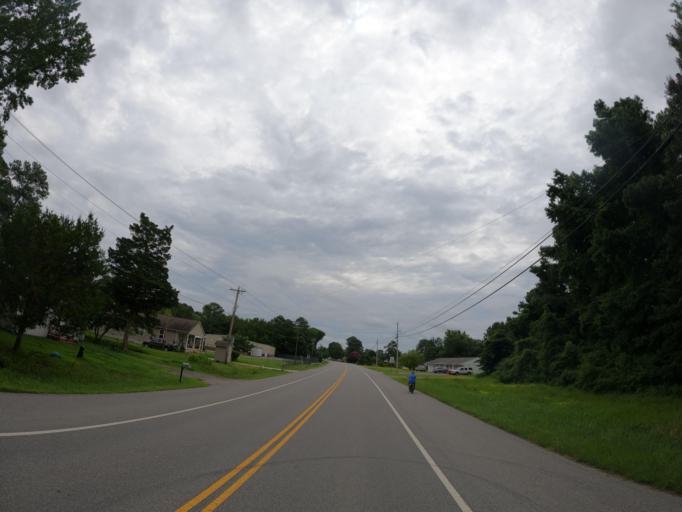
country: US
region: Maryland
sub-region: Saint Mary's County
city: Lexington Park
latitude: 38.1452
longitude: -76.5108
